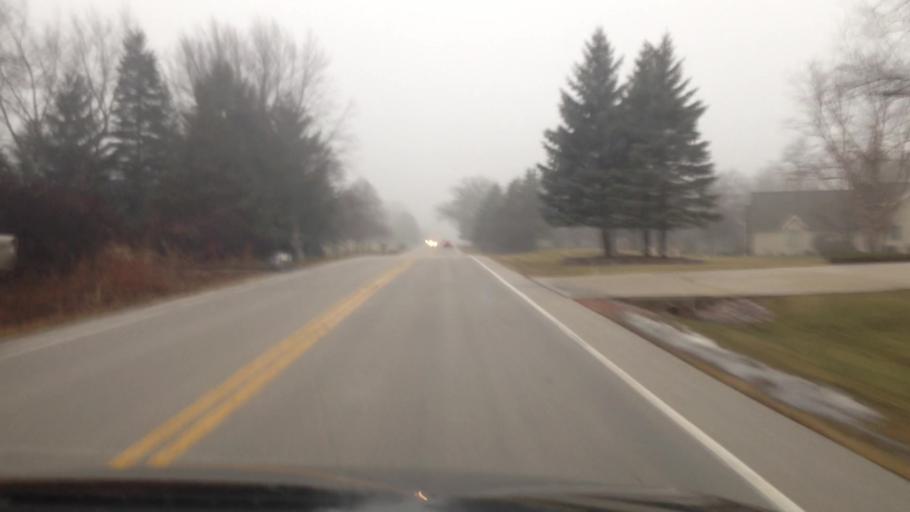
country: US
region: Wisconsin
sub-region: Milwaukee County
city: Hales Corners
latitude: 42.9136
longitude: -88.0866
